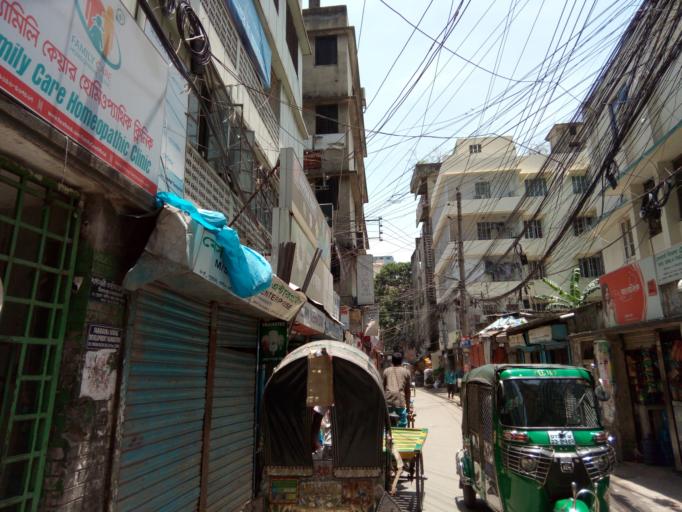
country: BD
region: Dhaka
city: Paltan
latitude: 23.7335
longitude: 90.4120
